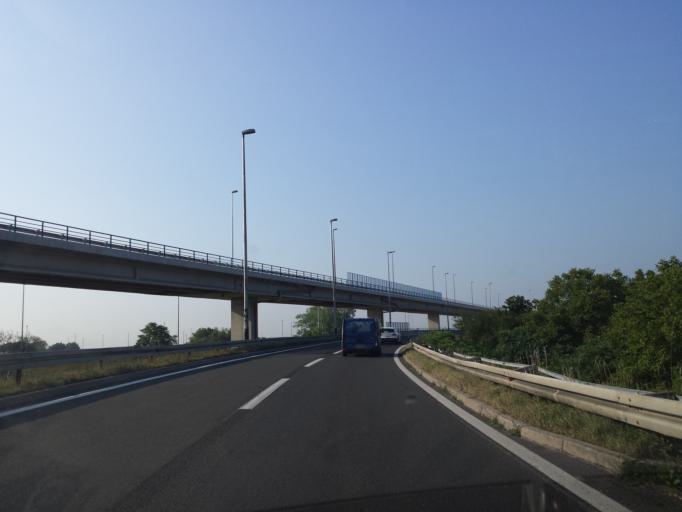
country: HR
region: Grad Zagreb
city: Lucko
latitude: 45.7607
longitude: 15.8972
